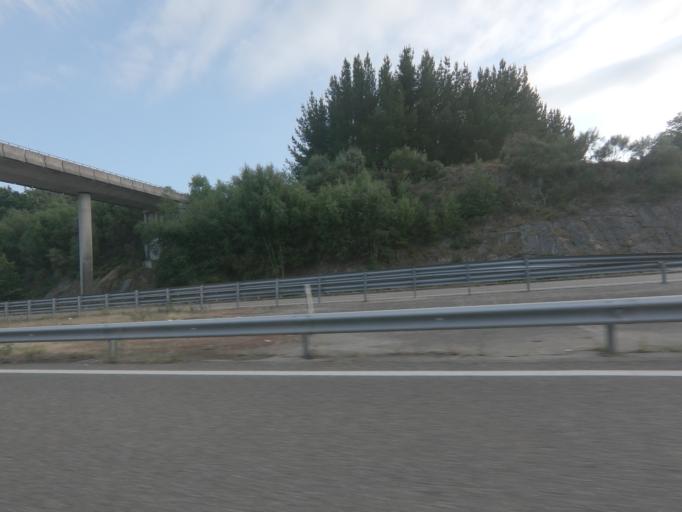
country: ES
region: Galicia
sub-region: Provincia de Ourense
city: Allariz
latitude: 42.2004
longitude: -7.7846
